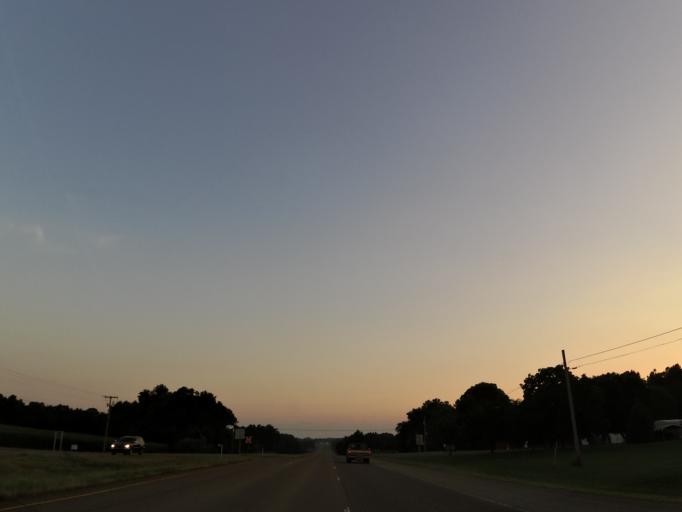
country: US
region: Tennessee
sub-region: Carroll County
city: McKenzie
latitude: 36.1640
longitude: -88.4570
